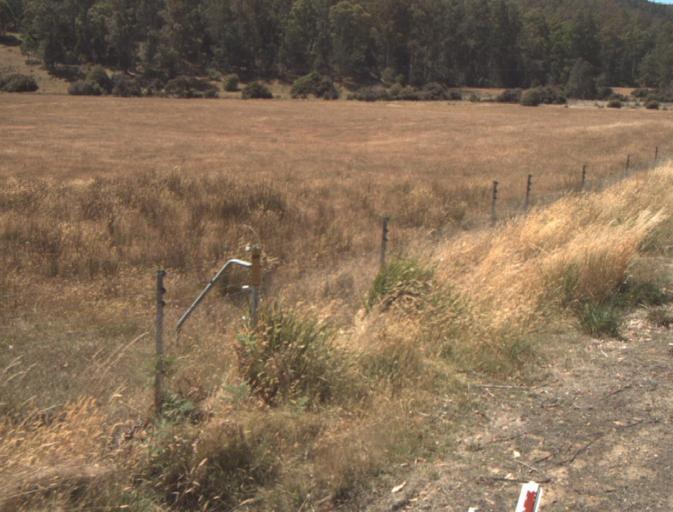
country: AU
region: Tasmania
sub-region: Dorset
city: Scottsdale
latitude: -41.3143
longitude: 147.3777
